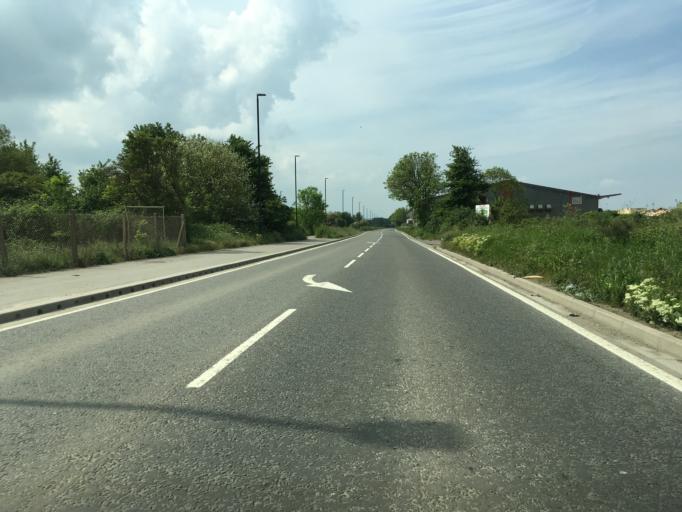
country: GB
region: England
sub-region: South Gloucestershire
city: Severn Beach
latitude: 51.5312
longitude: -2.6733
